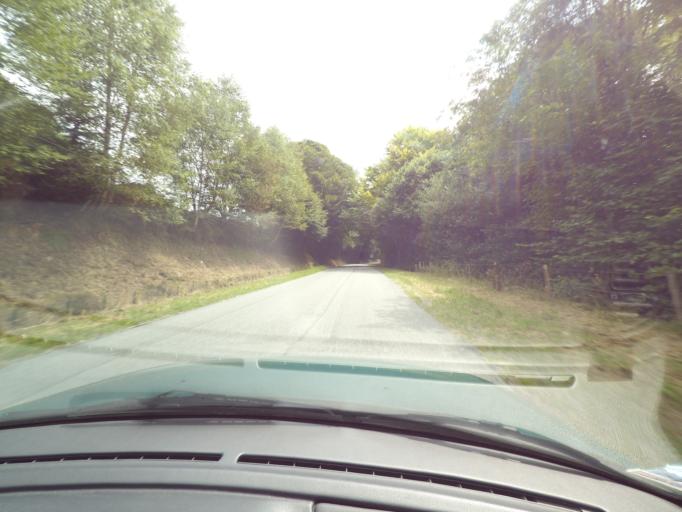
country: FR
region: Limousin
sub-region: Departement de la Correze
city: Bugeat
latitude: 45.7180
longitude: 2.0071
